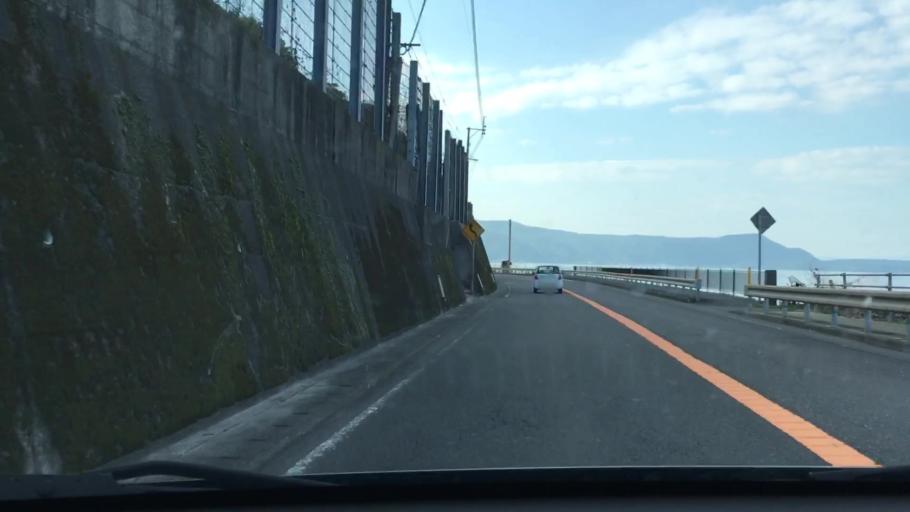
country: JP
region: Kagoshima
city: Hamanoichi
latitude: 31.6036
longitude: 130.7871
